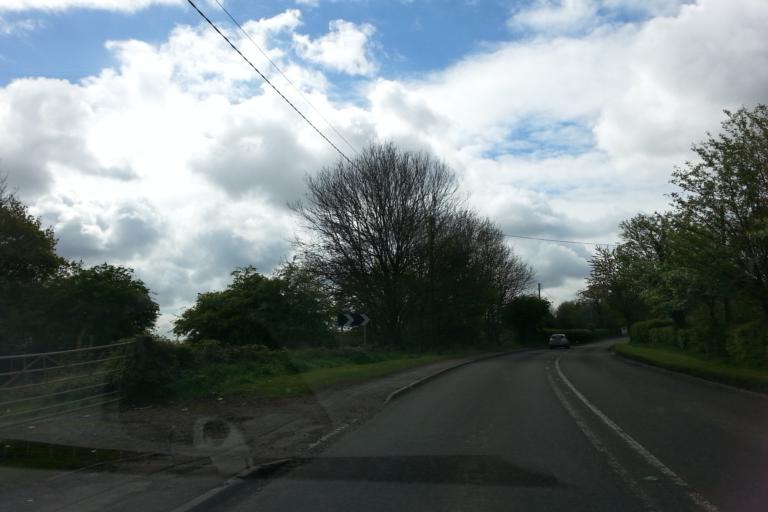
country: GB
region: England
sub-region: Staffordshire
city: Essington
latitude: 52.6307
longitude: -2.0447
